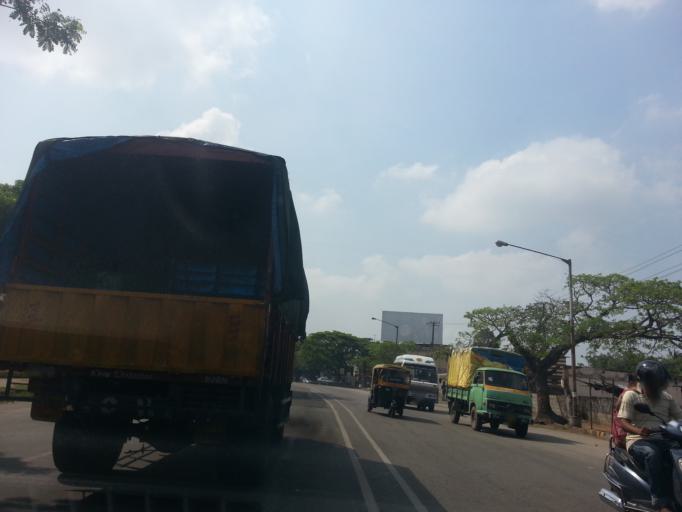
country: IN
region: Karnataka
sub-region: Mysore
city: Mysore
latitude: 12.3265
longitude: 76.6446
